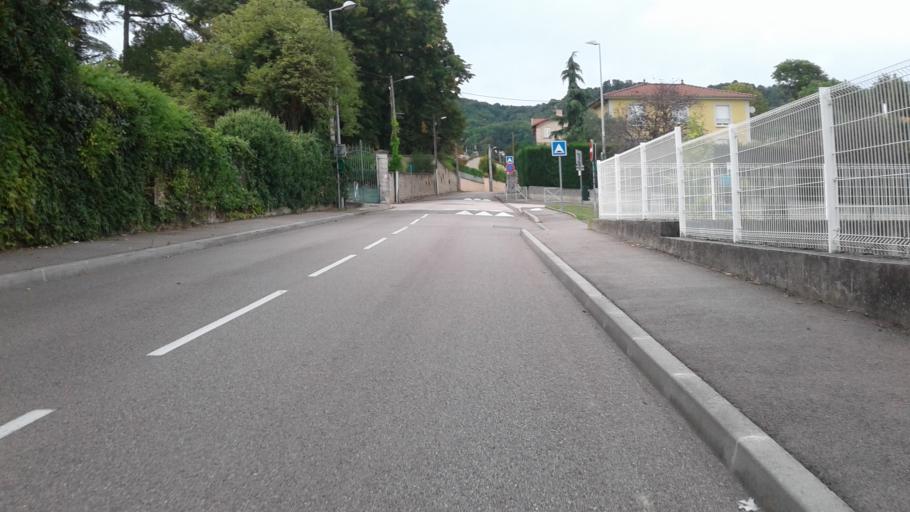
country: FR
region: Rhone-Alpes
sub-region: Departement de l'Ain
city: Beynost
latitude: 45.8350
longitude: 4.9965
